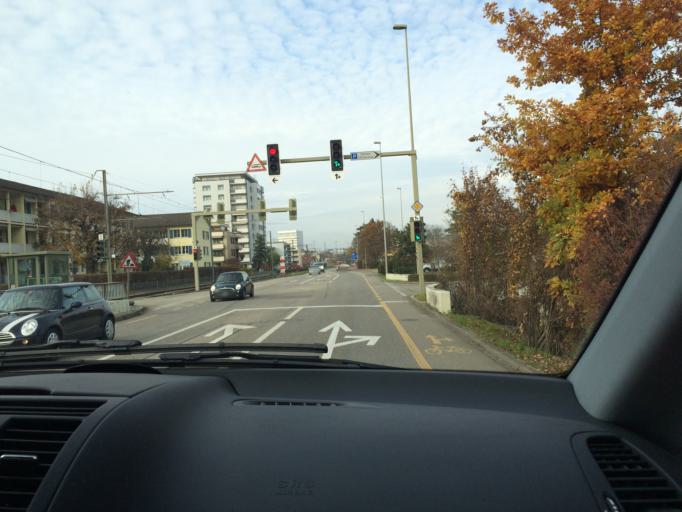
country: CH
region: Basel-Landschaft
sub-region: Bezirk Arlesheim
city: Munchenstein
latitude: 47.5251
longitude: 7.6165
